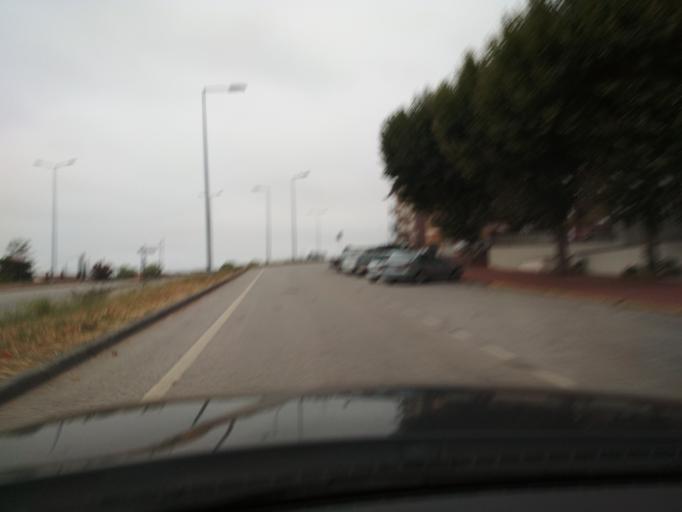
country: PT
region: Coimbra
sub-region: Coimbra
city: Coimbra
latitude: 40.1933
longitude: -8.4200
